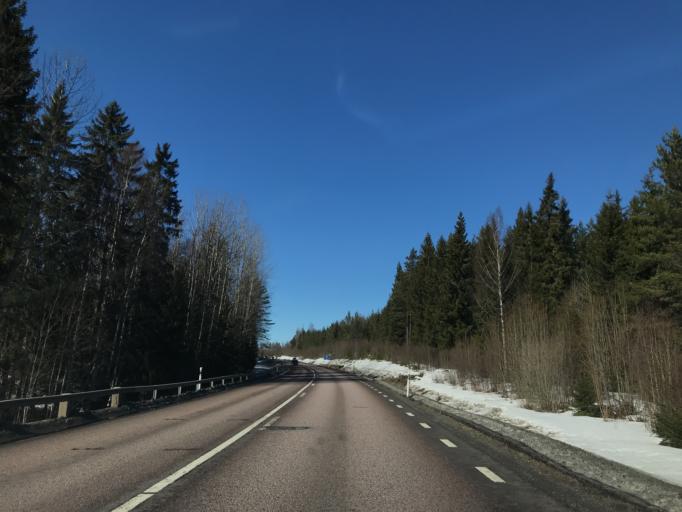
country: SE
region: Vaermland
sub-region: Filipstads Kommun
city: Filipstad
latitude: 59.6807
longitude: 14.2057
